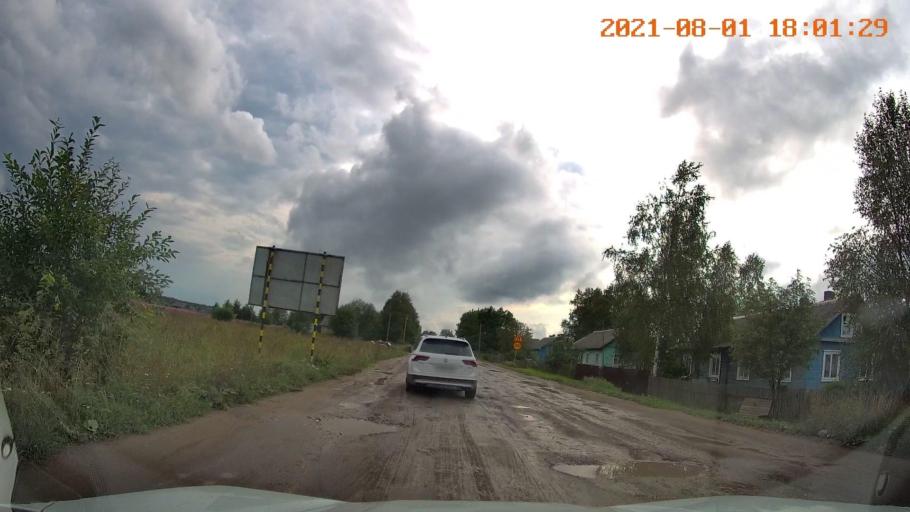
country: RU
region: Leningrad
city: Voznesen'ye
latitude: 60.8346
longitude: 35.7589
